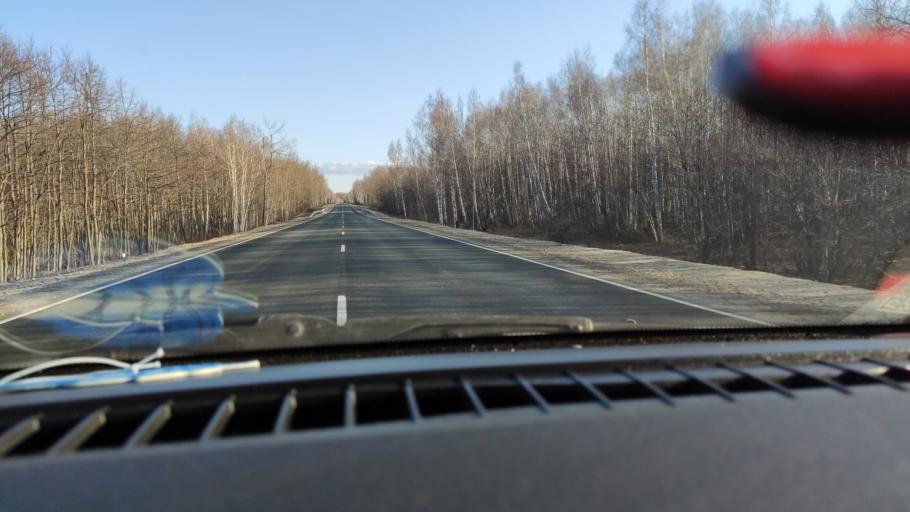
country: RU
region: Saratov
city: Khvalynsk
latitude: 52.4321
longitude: 48.0089
